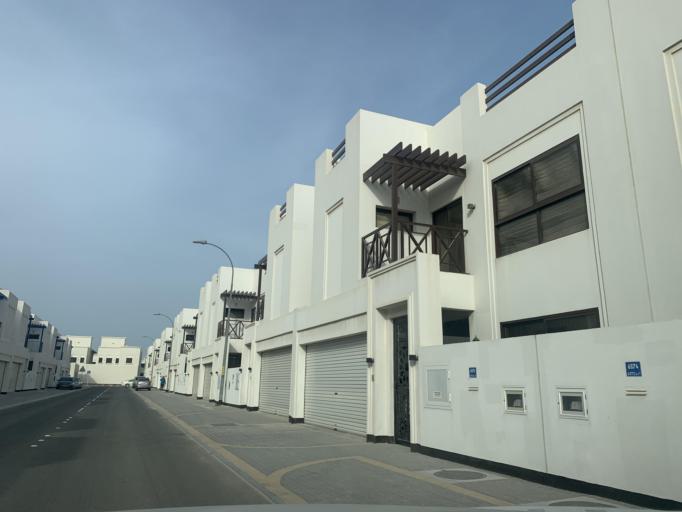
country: BH
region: Muharraq
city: Al Muharraq
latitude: 26.3148
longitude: 50.6280
